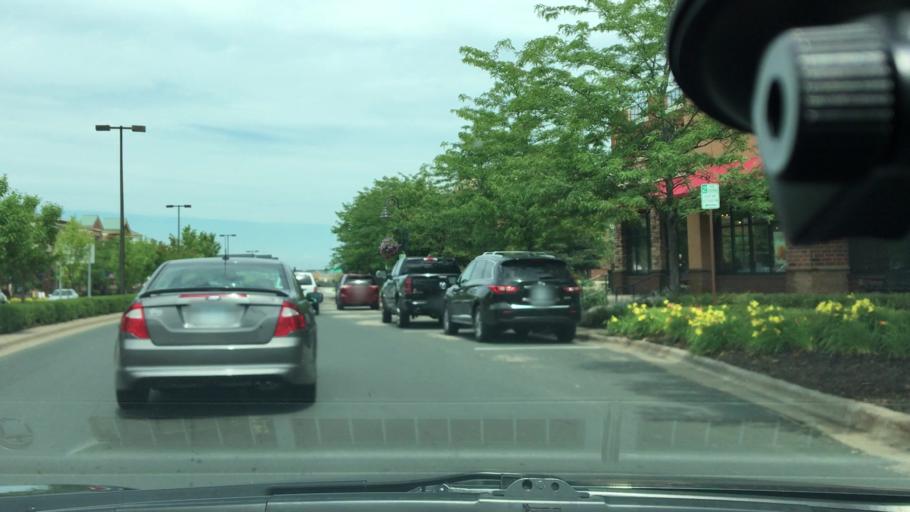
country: US
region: Minnesota
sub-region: Hennepin County
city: Maple Grove
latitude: 45.0928
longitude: -93.4268
